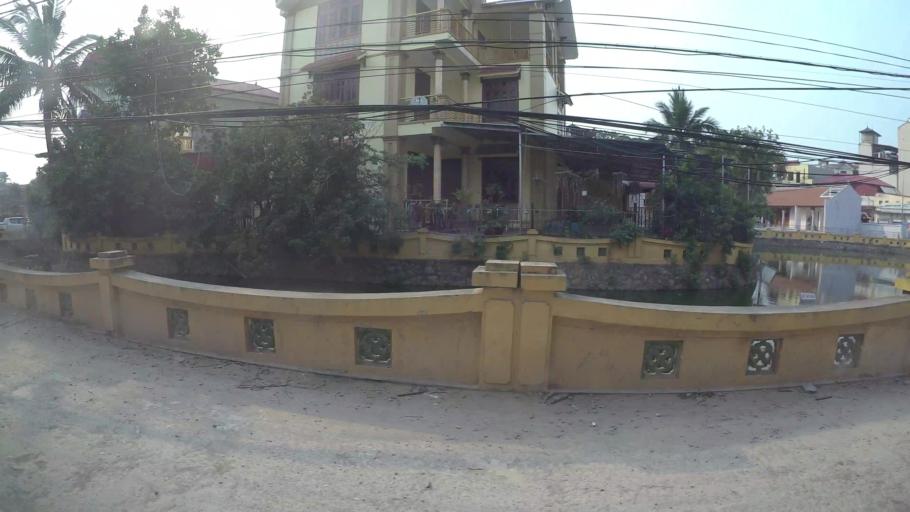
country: VN
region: Ha Noi
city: Cau Dien
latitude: 21.0010
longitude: 105.7466
